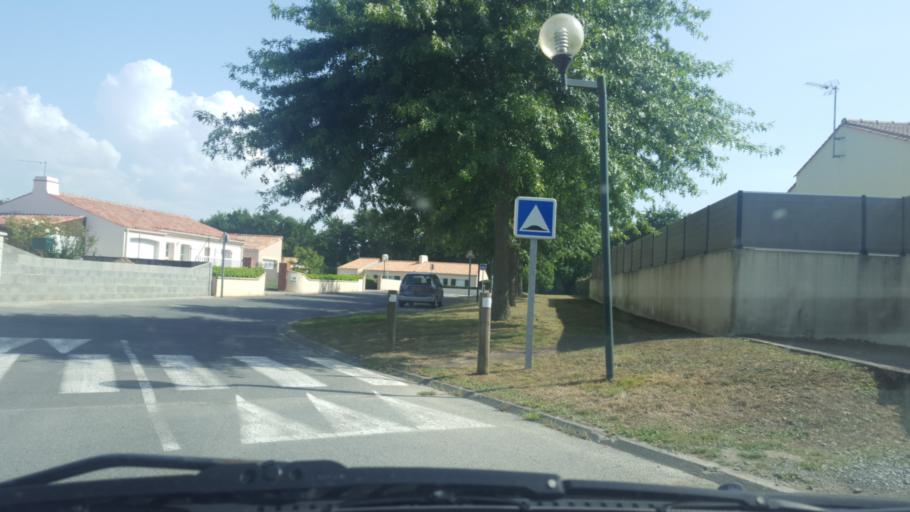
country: FR
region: Pays de la Loire
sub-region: Departement de la Loire-Atlantique
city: Saint-Philbert-de-Grand-Lieu
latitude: 47.0361
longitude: -1.6493
